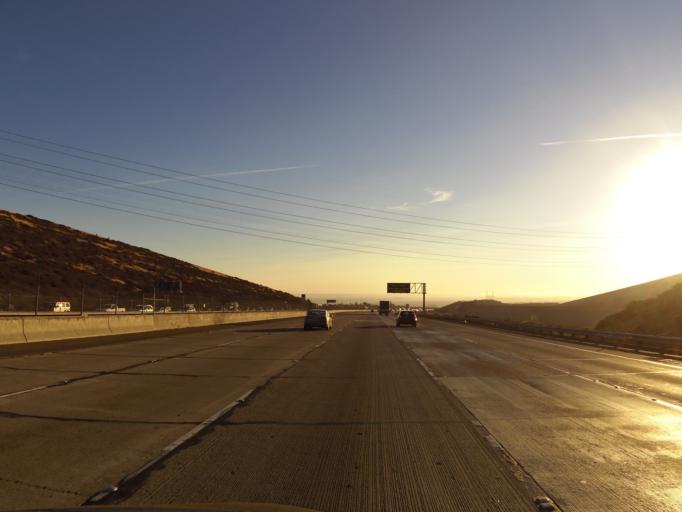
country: US
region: California
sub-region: Contra Costa County
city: Bay Point
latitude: 38.0215
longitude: -121.9810
